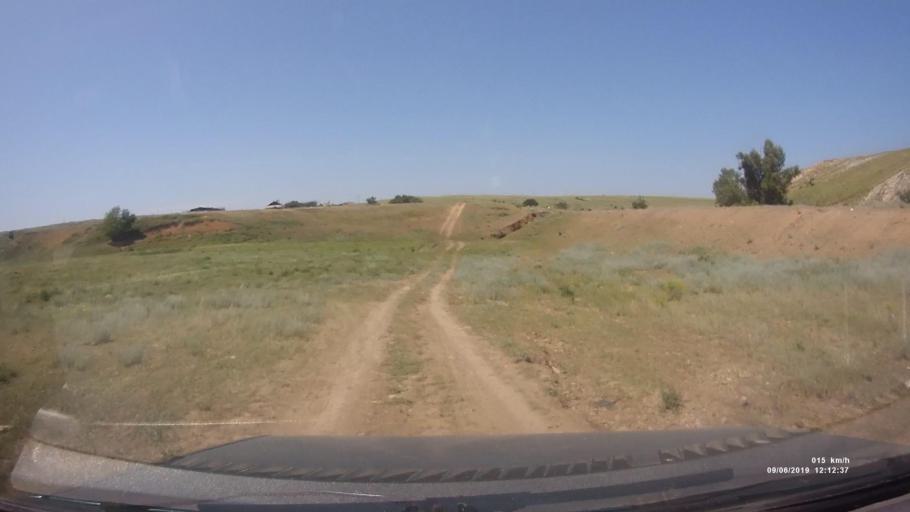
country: RU
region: Rostov
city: Staraya Stanitsa
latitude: 48.2507
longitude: 40.3281
